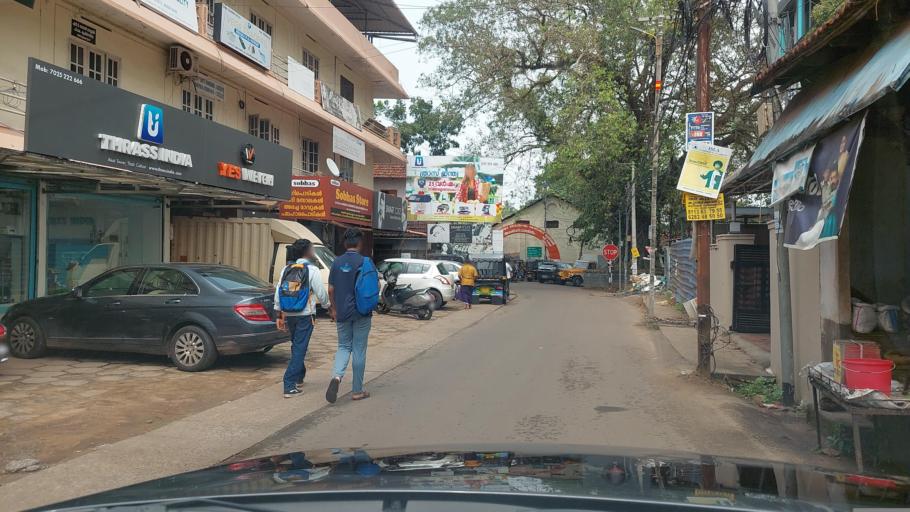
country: IN
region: Kerala
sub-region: Kozhikode
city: Kozhikode
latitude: 11.2472
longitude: 75.7883
